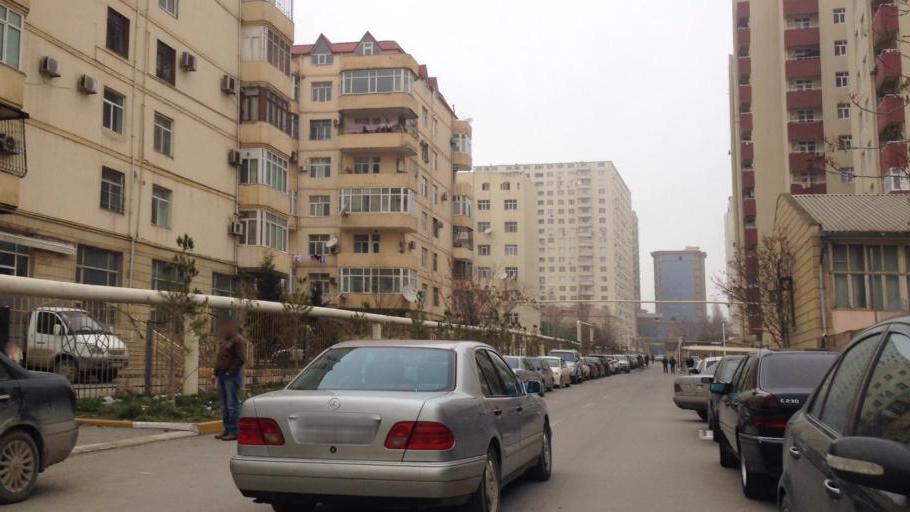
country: AZ
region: Baki
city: Baku
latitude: 40.3851
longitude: 49.8723
